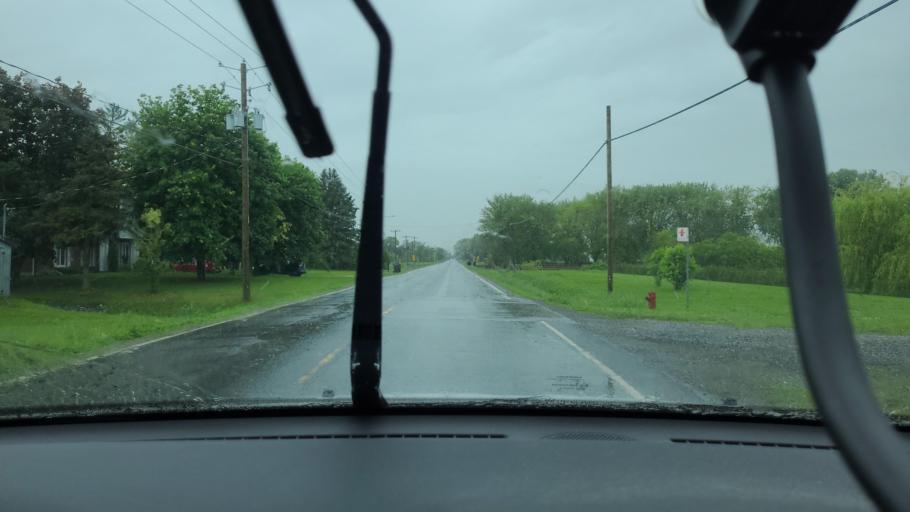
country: CA
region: Quebec
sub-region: Monteregie
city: Saint-Hyacinthe
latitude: 45.6165
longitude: -73.0277
